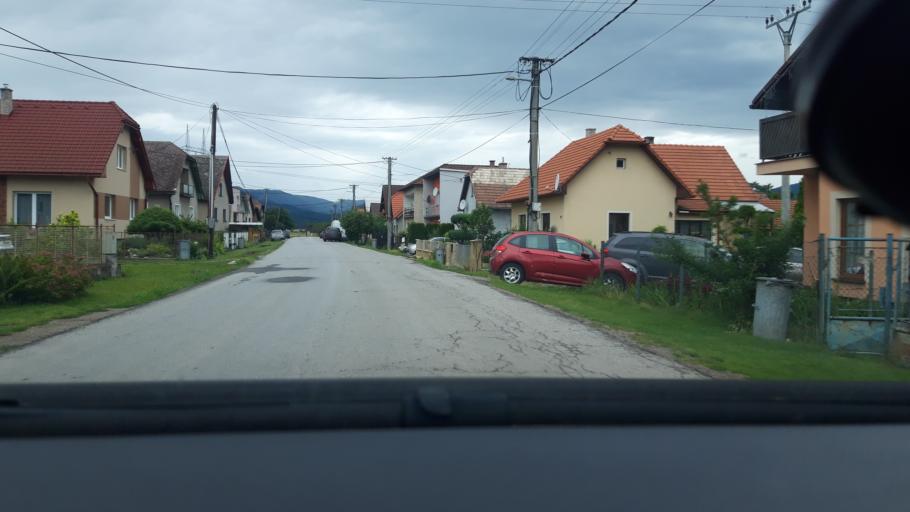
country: SK
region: Zilinsky
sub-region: Okres Martin
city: Martin
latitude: 48.9771
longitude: 18.9102
